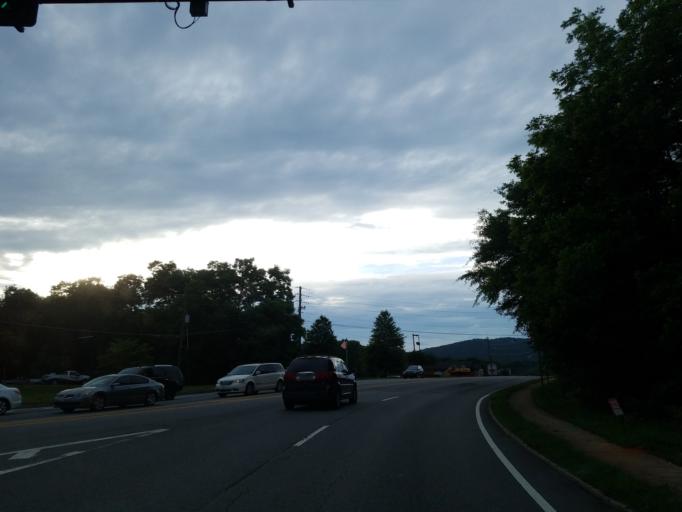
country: US
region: Georgia
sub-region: Forsyth County
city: Cumming
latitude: 34.2074
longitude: -84.1424
